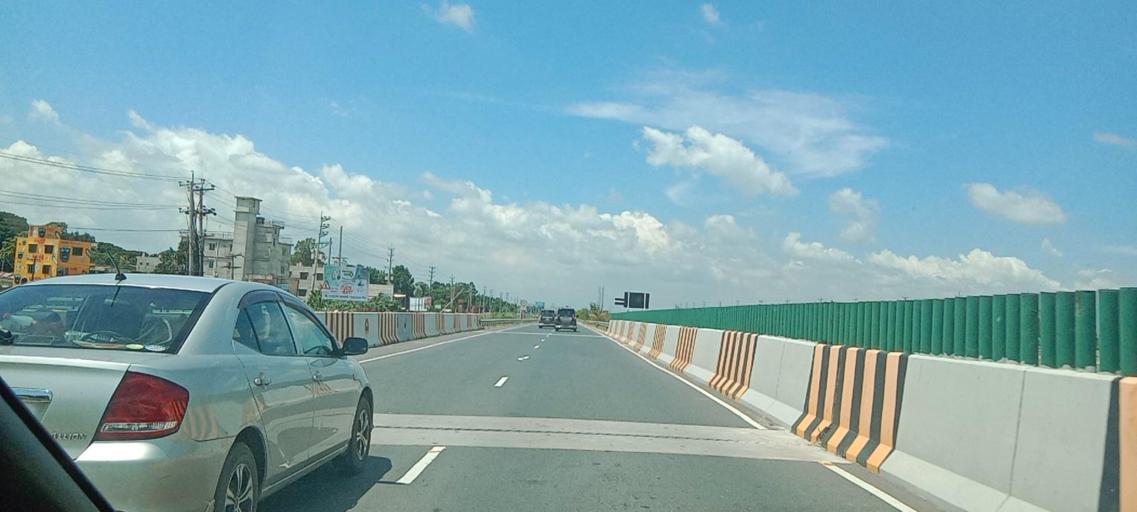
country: BD
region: Dhaka
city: Dohar
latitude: 23.4977
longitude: 90.2717
